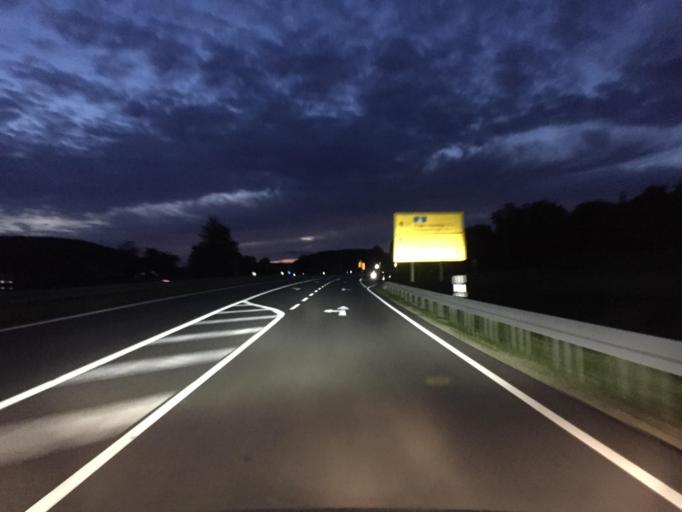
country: DE
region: Baden-Wuerttemberg
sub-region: Freiburg Region
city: Blumberg
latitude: 47.8624
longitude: 8.5457
